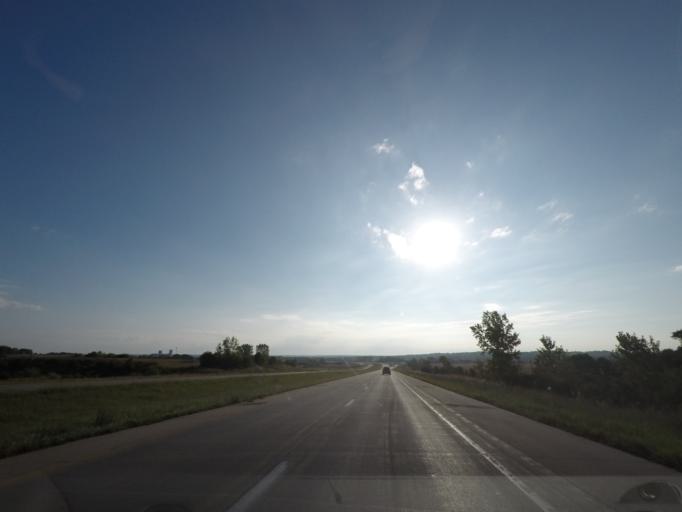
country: US
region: Iowa
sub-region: Warren County
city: Carlisle
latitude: 41.5115
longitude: -93.5370
